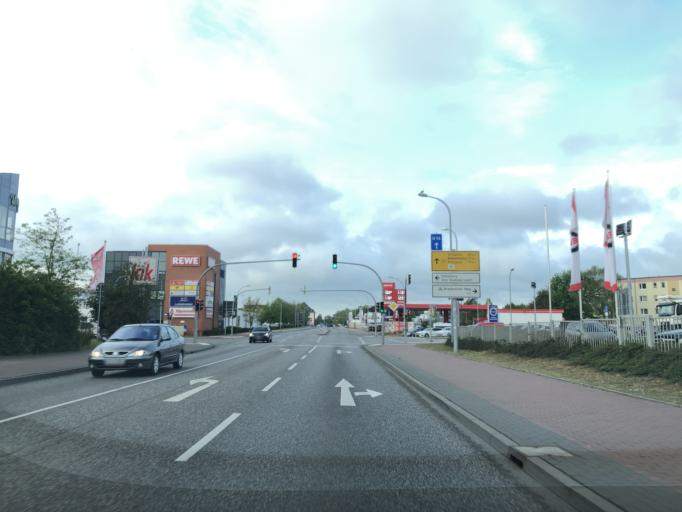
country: DE
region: Mecklenburg-Vorpommern
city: Guestrow
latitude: 53.8094
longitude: 12.1888
